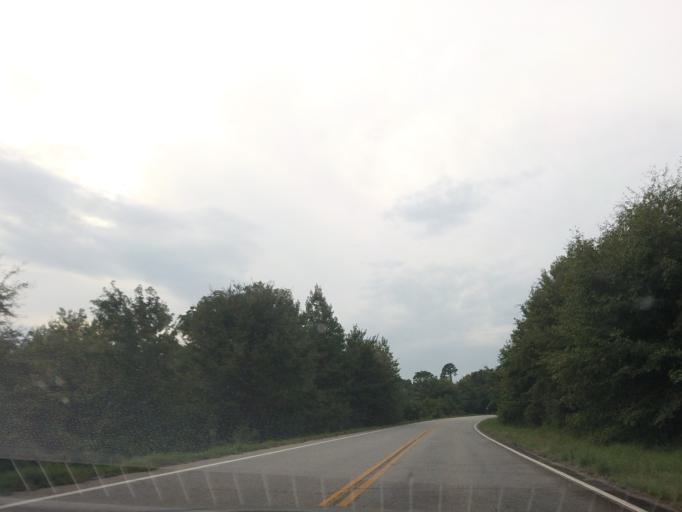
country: US
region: Georgia
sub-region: Twiggs County
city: Jeffersonville
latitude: 32.6916
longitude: -83.3718
